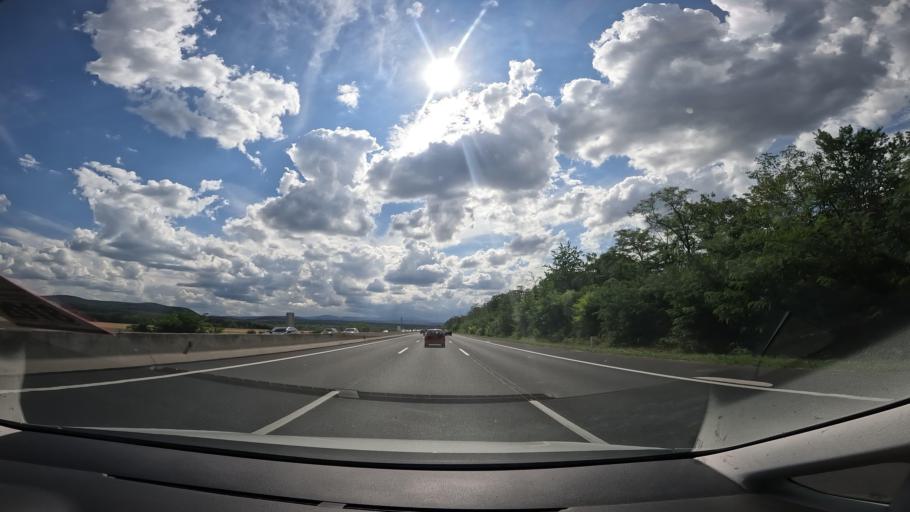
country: AT
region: Lower Austria
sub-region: Politischer Bezirk Neunkirchen
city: Breitenau
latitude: 47.7293
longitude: 16.1568
